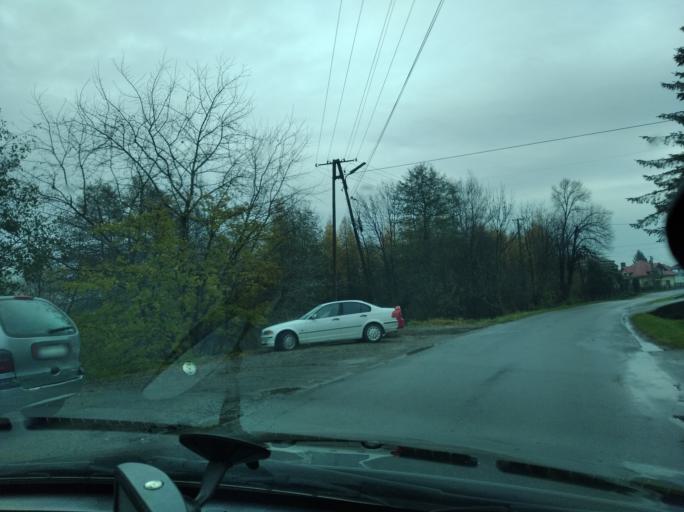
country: PL
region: Subcarpathian Voivodeship
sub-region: Powiat strzyzowski
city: Czudec
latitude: 49.9361
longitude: 21.8448
